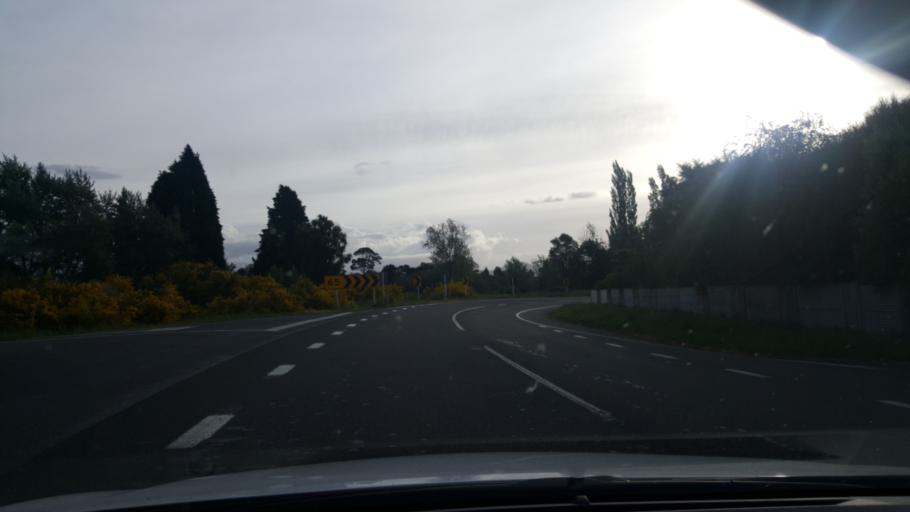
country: NZ
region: Waikato
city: Turangi
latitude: -38.9116
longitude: 175.9029
